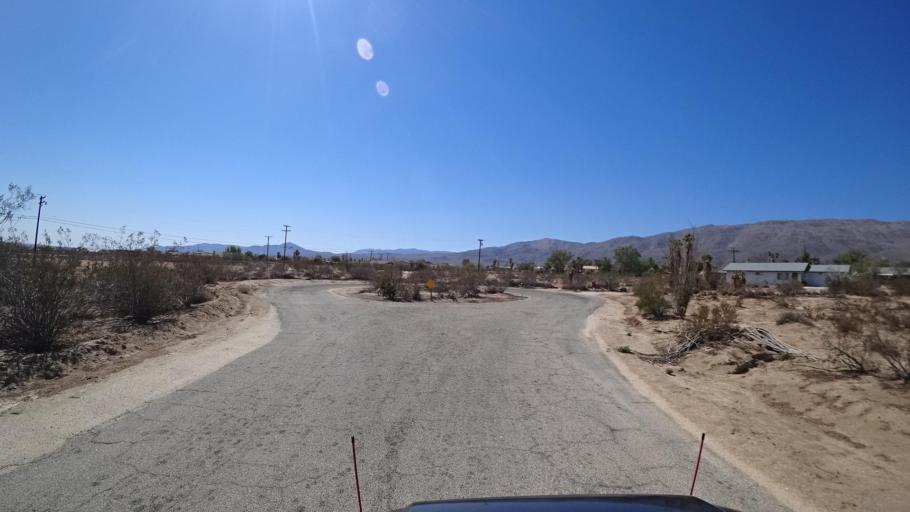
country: US
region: California
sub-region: San Diego County
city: Borrego Springs
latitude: 33.2290
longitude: -116.3705
